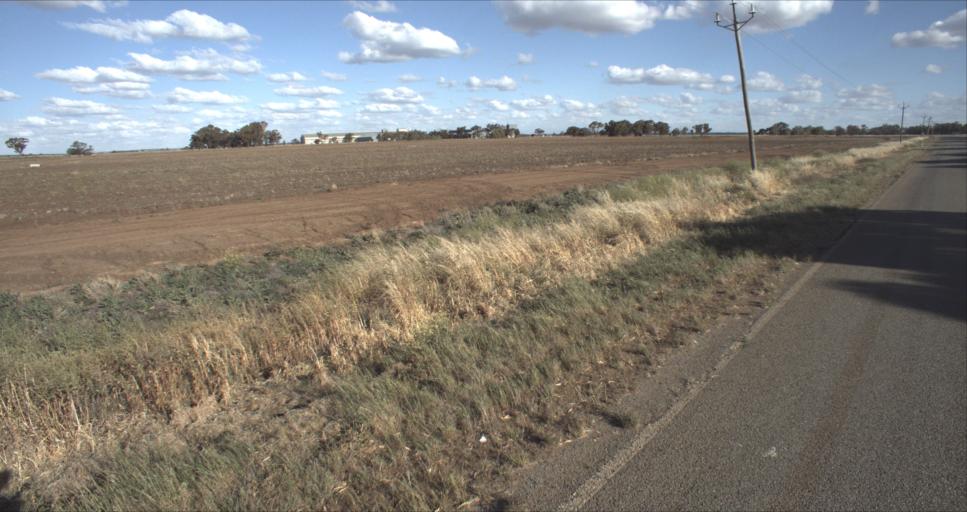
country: AU
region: New South Wales
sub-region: Leeton
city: Leeton
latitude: -34.5499
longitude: 146.2792
